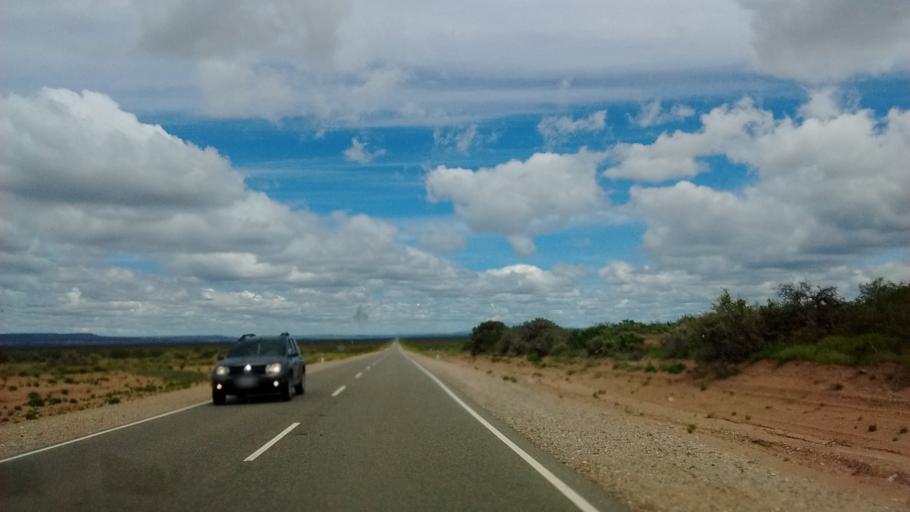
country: AR
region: Neuquen
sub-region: Departamento de Picun Leufu
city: Picun Leufu
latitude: -39.7860
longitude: -69.6641
